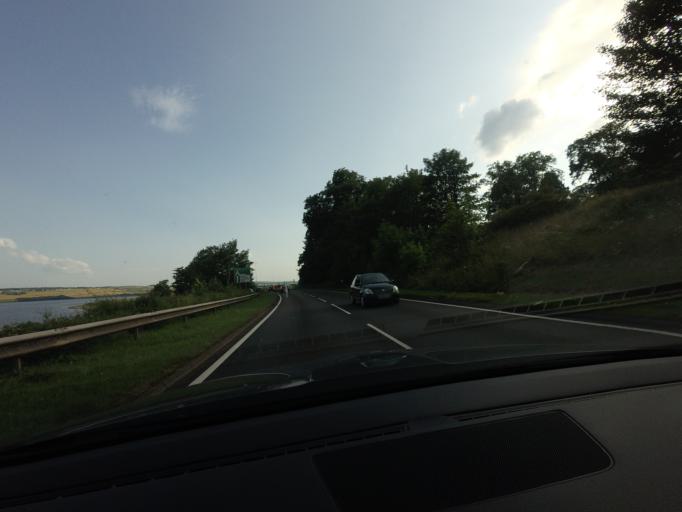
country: GB
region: Scotland
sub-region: Highland
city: Evanton
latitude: 57.6295
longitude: -4.3668
